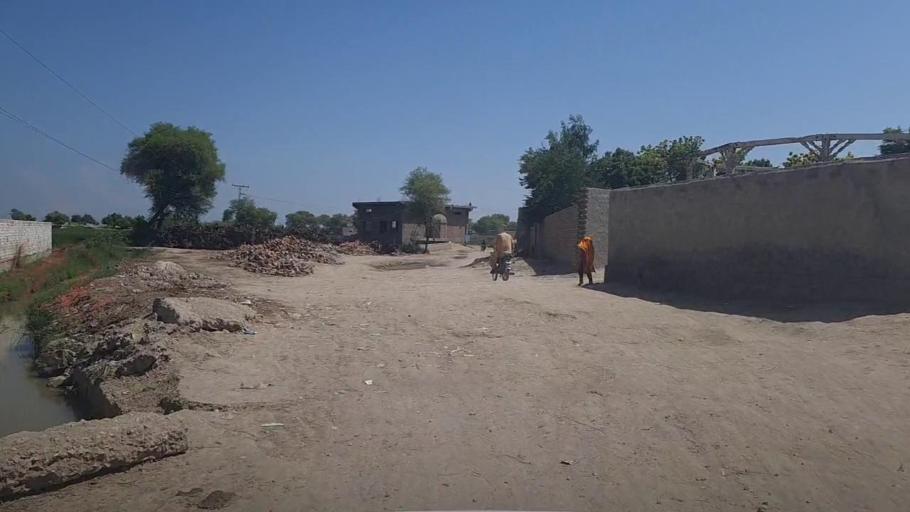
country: PK
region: Sindh
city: Kashmor
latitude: 28.3006
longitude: 69.4242
